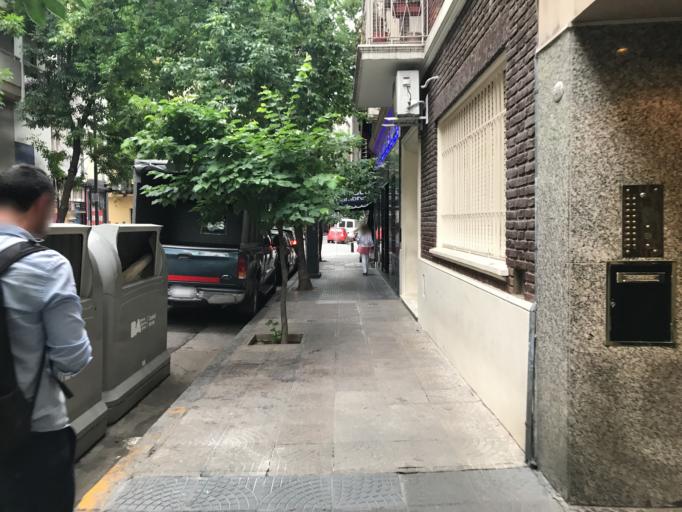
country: AR
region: Buenos Aires F.D.
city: Retiro
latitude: -34.5925
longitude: -58.4029
